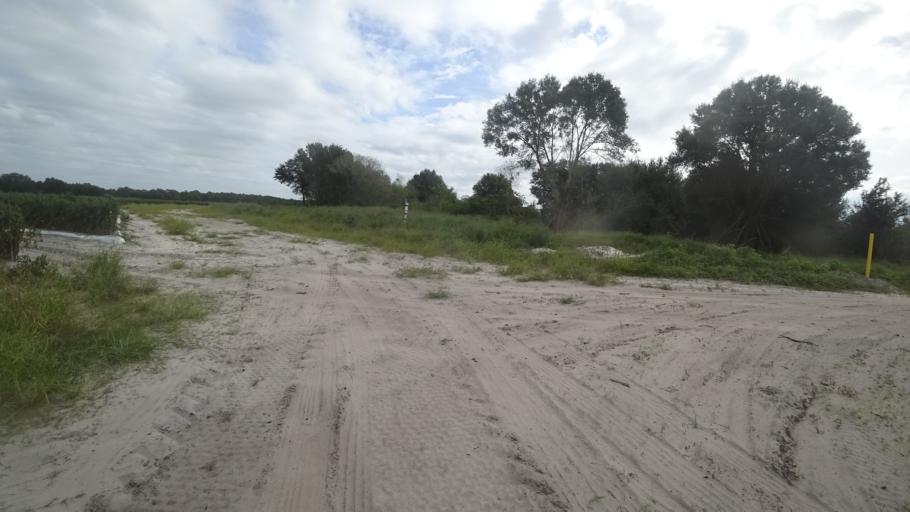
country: US
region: Florida
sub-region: Hillsborough County
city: Wimauma
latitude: 27.5852
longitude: -82.3074
